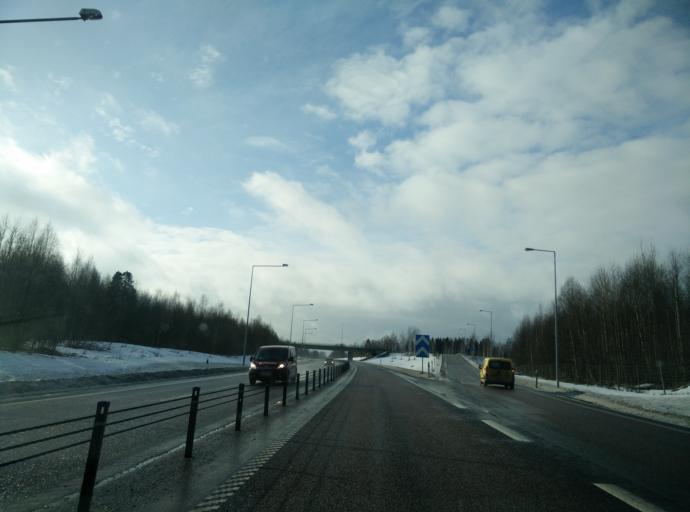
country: SE
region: Gaevleborg
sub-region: Sandvikens Kommun
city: Jarbo
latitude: 60.6057
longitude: 16.5915
